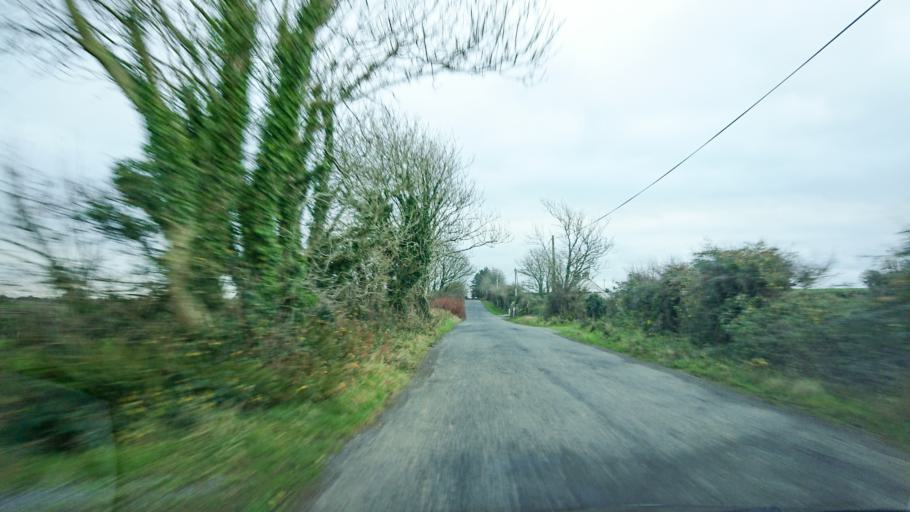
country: IE
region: Munster
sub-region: Waterford
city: Dunmore East
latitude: 52.2394
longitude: -6.9918
